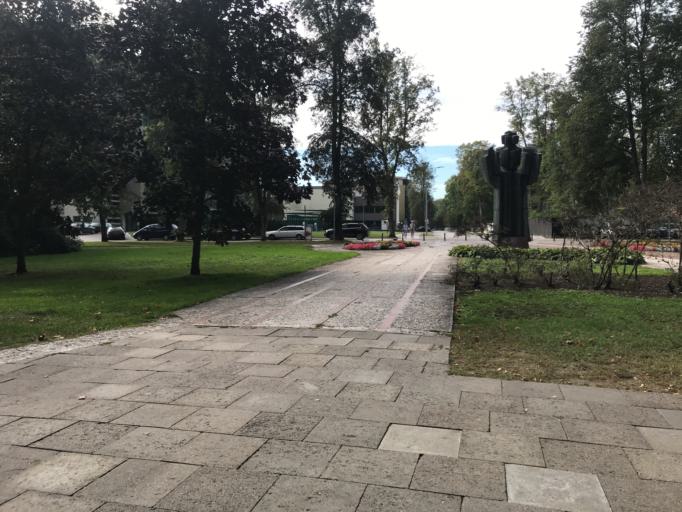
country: LT
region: Alytaus apskritis
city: Druskininkai
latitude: 54.0200
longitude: 23.9765
